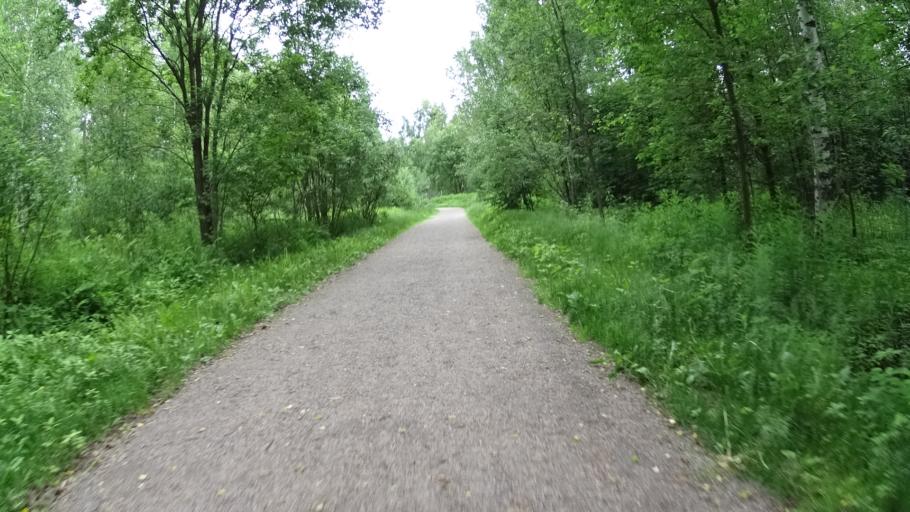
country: FI
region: Uusimaa
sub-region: Helsinki
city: Kilo
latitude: 60.1870
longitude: 24.7742
